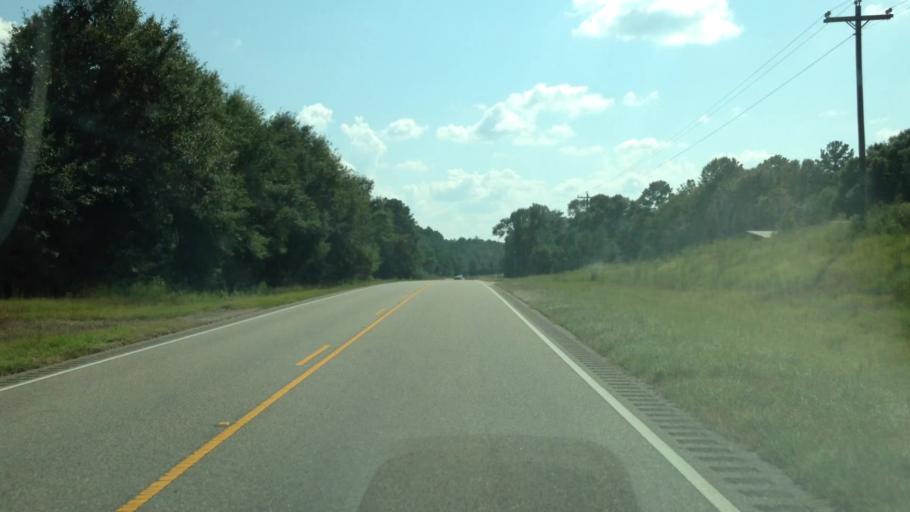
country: US
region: Alabama
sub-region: Covington County
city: Florala
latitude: 31.0603
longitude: -86.5759
